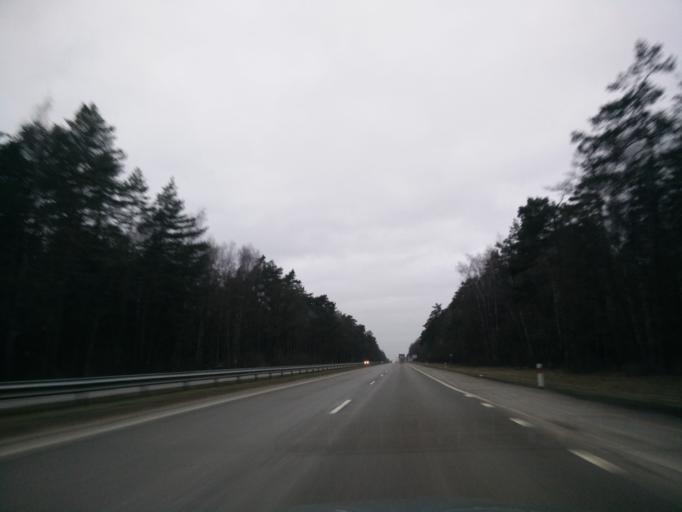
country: LT
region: Vilnius County
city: Lazdynai
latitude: 54.6472
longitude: 25.1690
